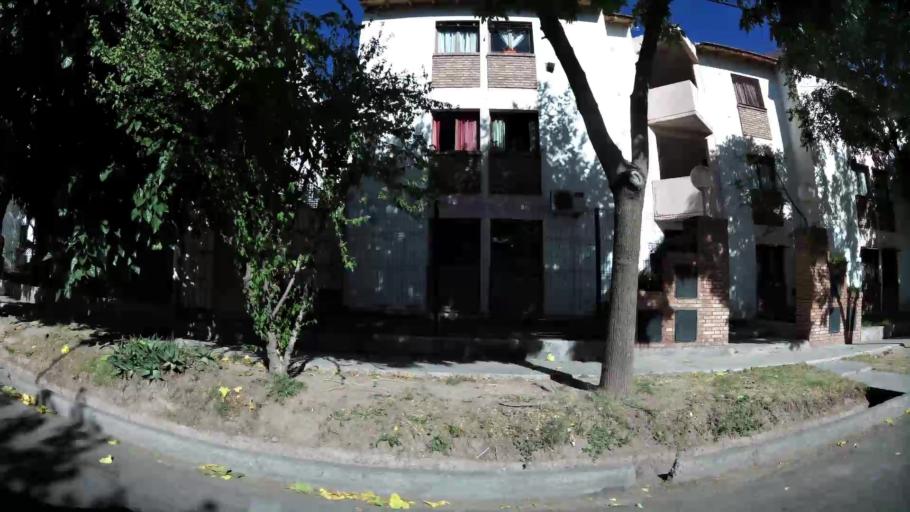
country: AR
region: Mendoza
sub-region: Departamento de Godoy Cruz
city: Godoy Cruz
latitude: -32.9322
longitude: -68.8610
